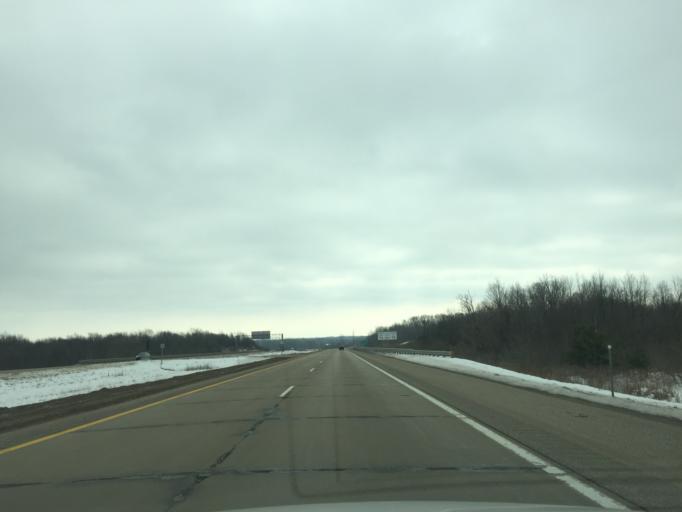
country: US
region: Michigan
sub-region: Ottawa County
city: Hudsonville
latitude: 42.8543
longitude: -85.8124
